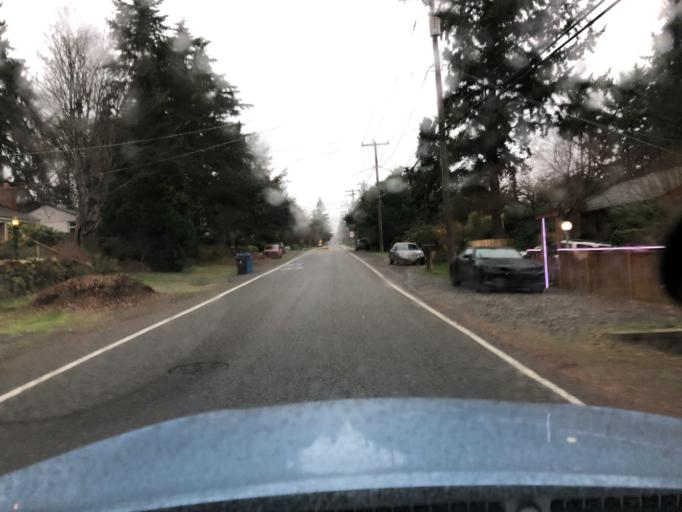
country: US
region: Washington
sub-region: King County
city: Lake Forest Park
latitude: 47.7363
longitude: -122.2992
